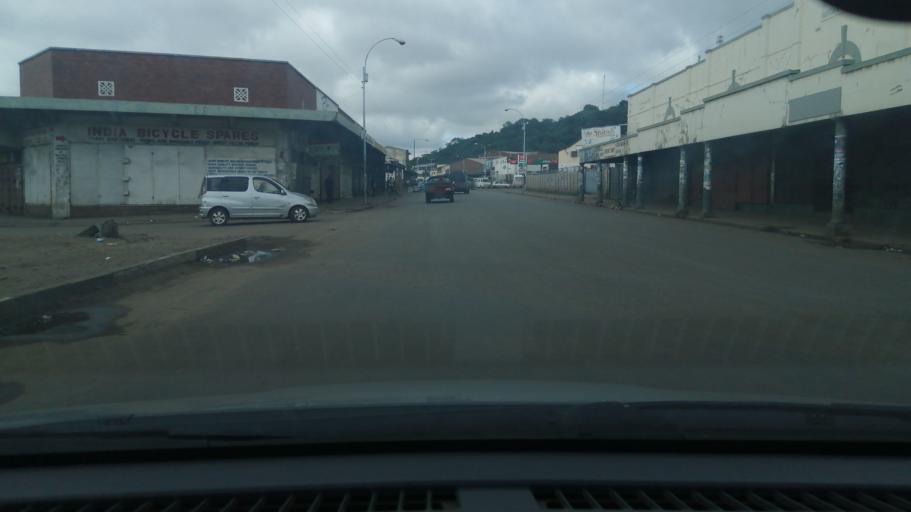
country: ZW
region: Harare
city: Harare
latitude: -17.8388
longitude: 31.0431
